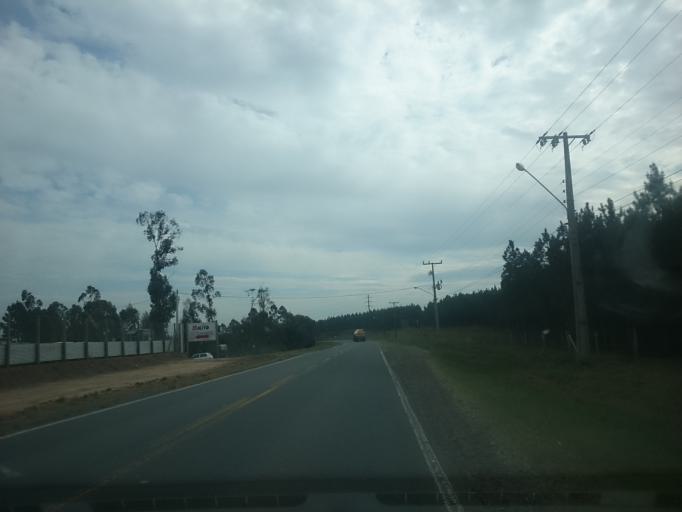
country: BR
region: Santa Catarina
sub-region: Lages
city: Lages
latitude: -27.7595
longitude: -50.3292
